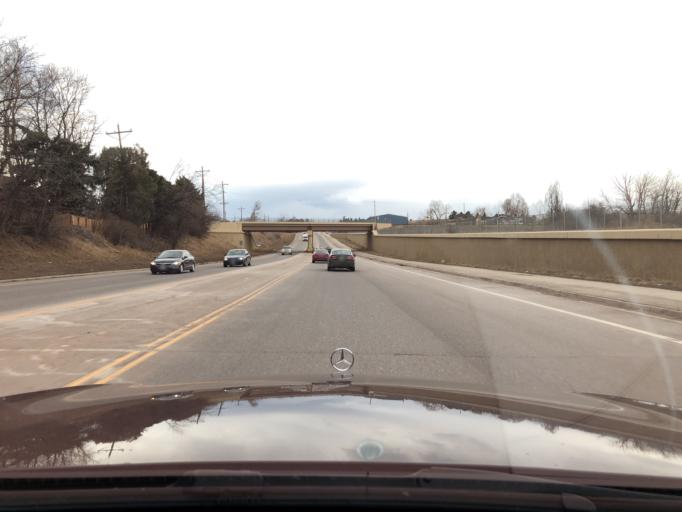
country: US
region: Colorado
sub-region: Boulder County
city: Gunbarrel
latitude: 40.0147
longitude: -105.1819
